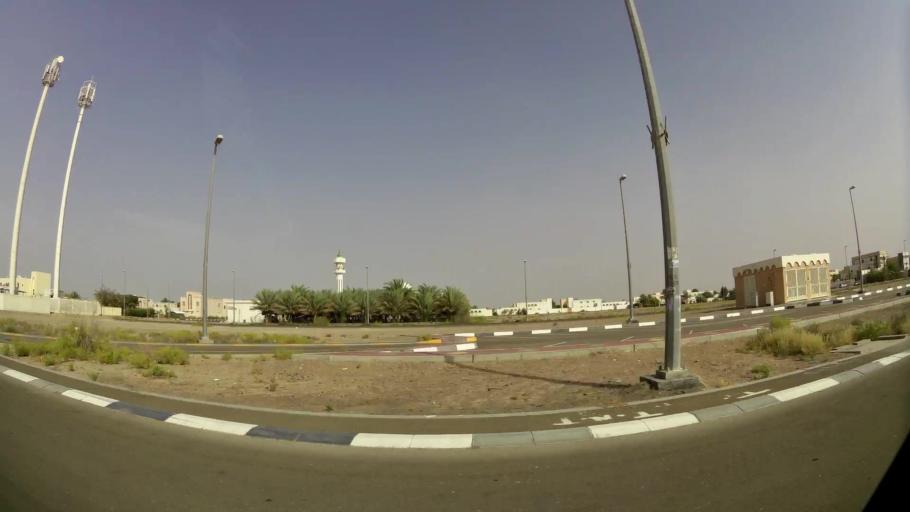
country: AE
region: Abu Dhabi
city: Al Ain
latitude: 24.2088
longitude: 55.5921
